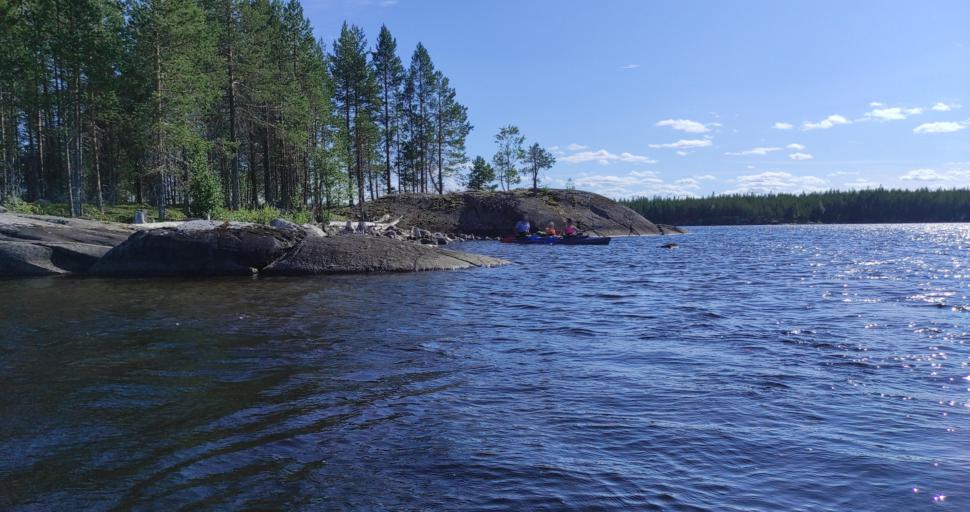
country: RU
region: Murmansk
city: Zelenoborskiy
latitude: 66.6571
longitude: 32.2532
